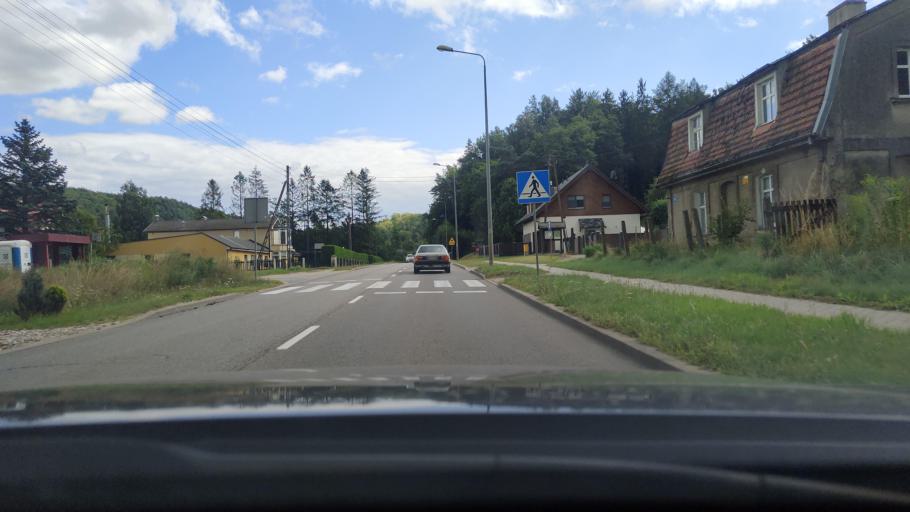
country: PL
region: Pomeranian Voivodeship
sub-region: Powiat wejherowski
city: Wejherowo
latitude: 54.5874
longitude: 18.2487
